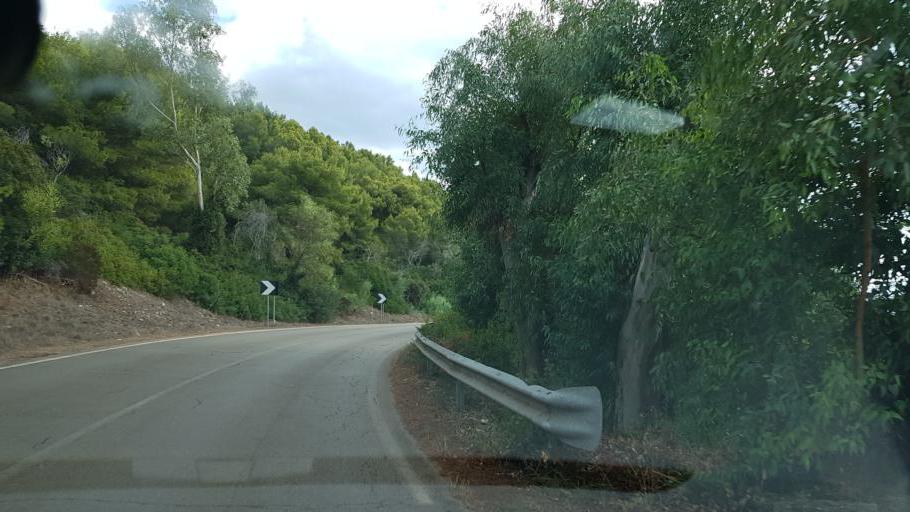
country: IT
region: Apulia
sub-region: Provincia di Lecce
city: Nardo
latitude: 40.1674
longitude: 17.9515
